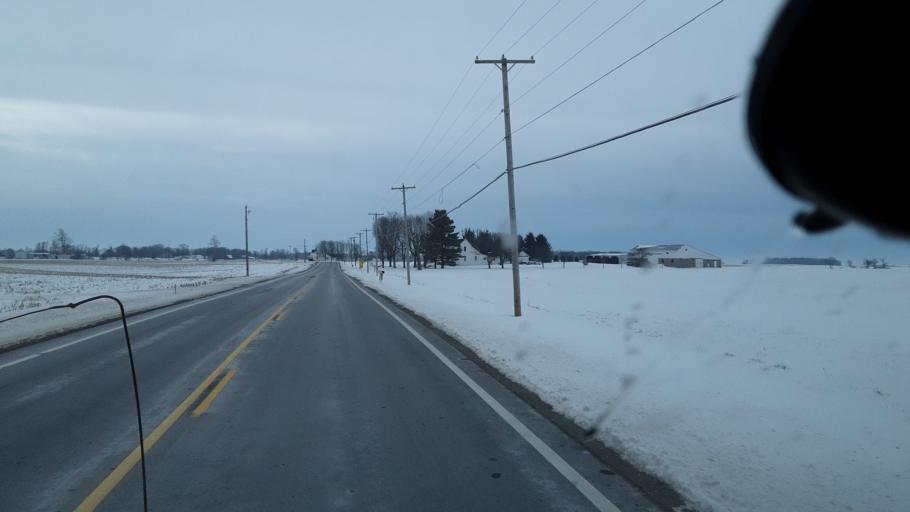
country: US
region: Ohio
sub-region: Madison County
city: London
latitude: 39.8604
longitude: -83.4614
